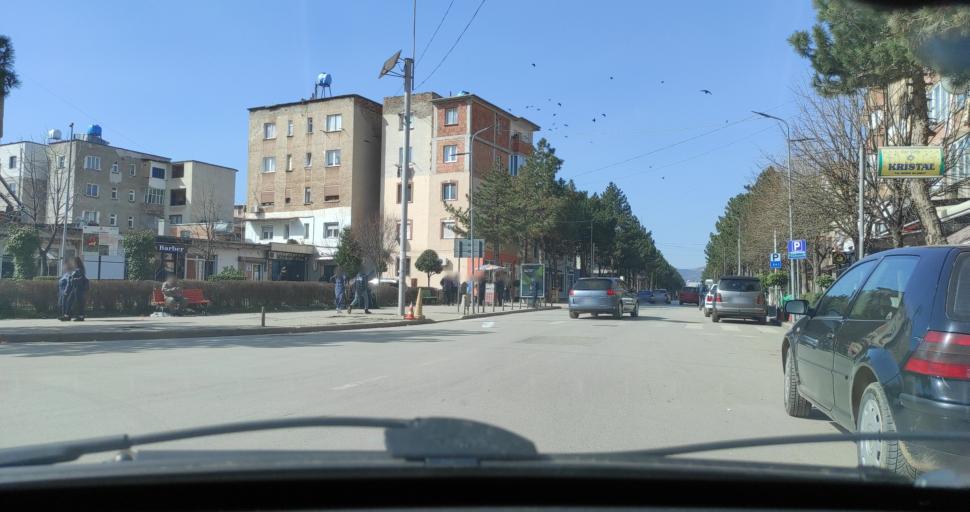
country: AL
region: Kukes
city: Kukes
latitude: 42.0758
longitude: 20.4223
